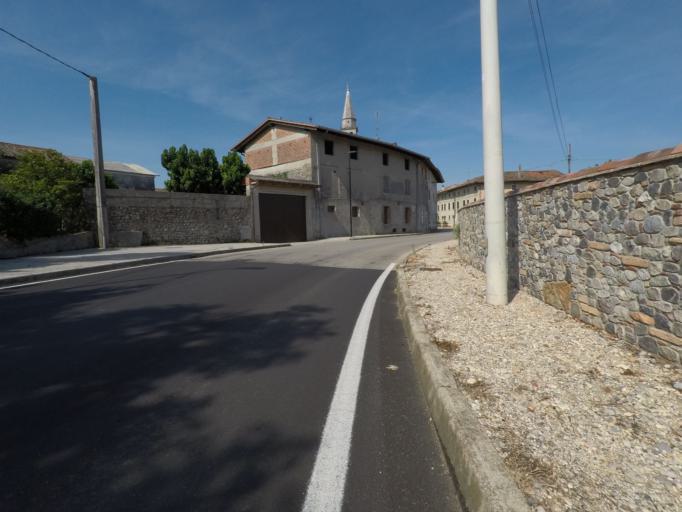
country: IT
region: Friuli Venezia Giulia
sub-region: Provincia di Udine
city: San Vito di Fagagna
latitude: 46.0677
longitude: 13.0831
